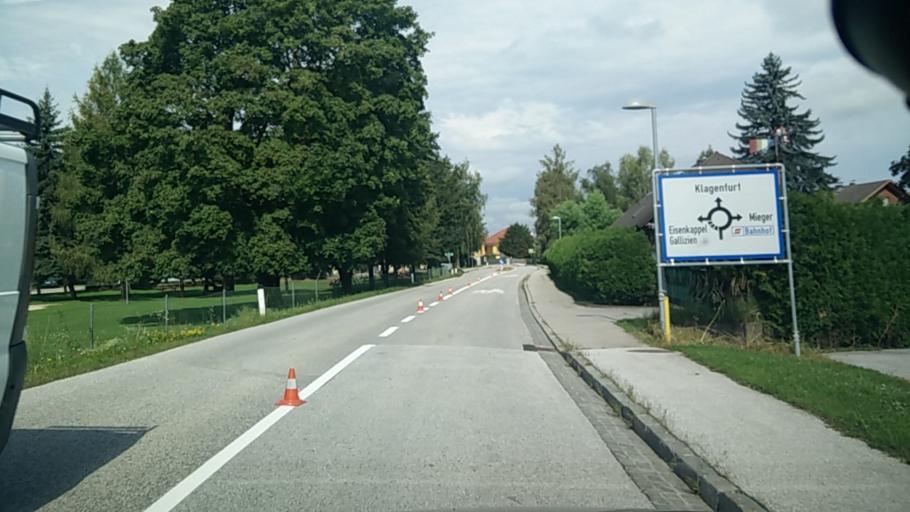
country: AT
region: Carinthia
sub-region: Politischer Bezirk Klagenfurt Land
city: Grafenstein
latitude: 46.6160
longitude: 14.4688
